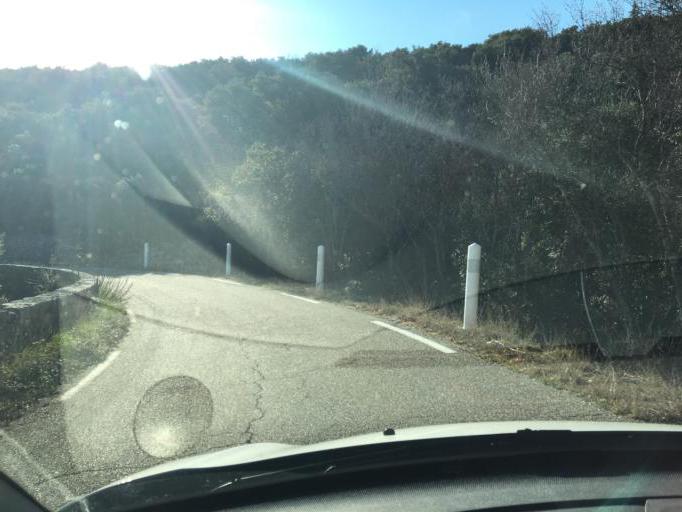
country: FR
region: Provence-Alpes-Cote d'Azur
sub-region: Departement du Vaucluse
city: Villes-sur-Auzon
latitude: 44.0422
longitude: 5.2689
